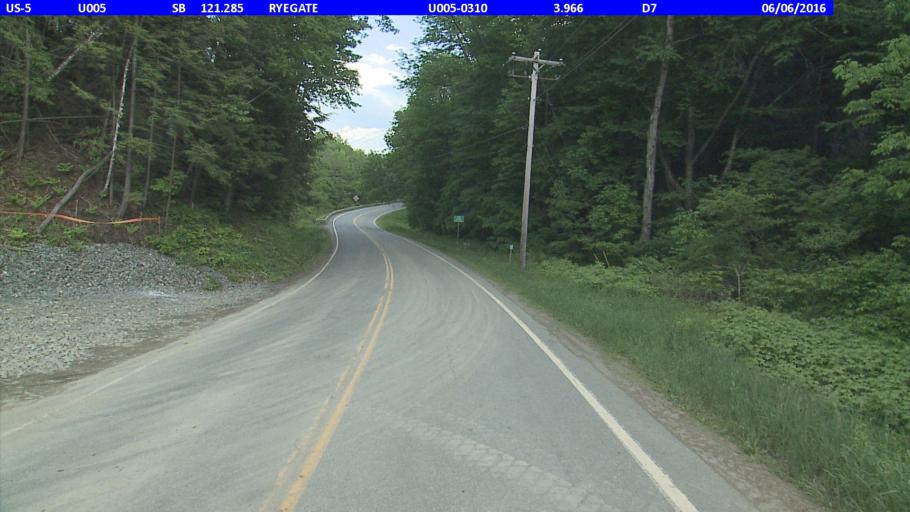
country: US
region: New Hampshire
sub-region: Grafton County
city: Woodsville
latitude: 44.2089
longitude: -72.0615
